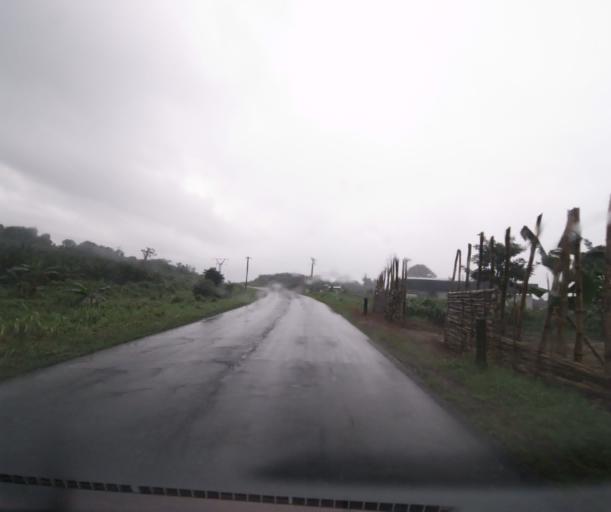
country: CM
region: South-West Province
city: Idenao
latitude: 4.1742
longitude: 8.9979
